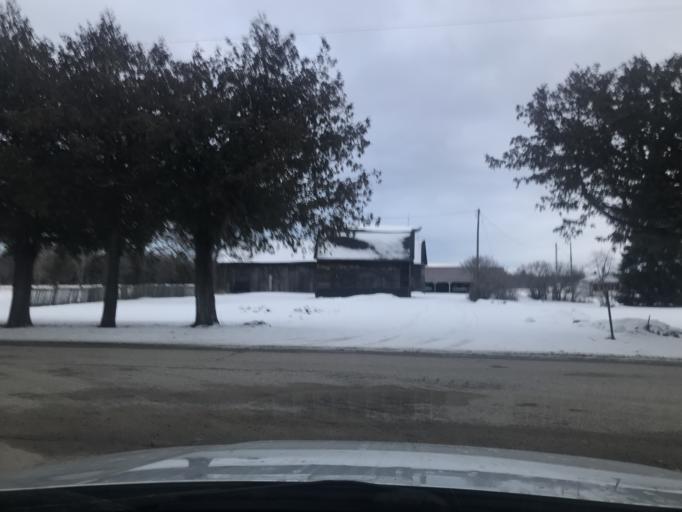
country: US
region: Wisconsin
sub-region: Marinette County
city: Marinette
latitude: 45.0481
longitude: -87.6474
